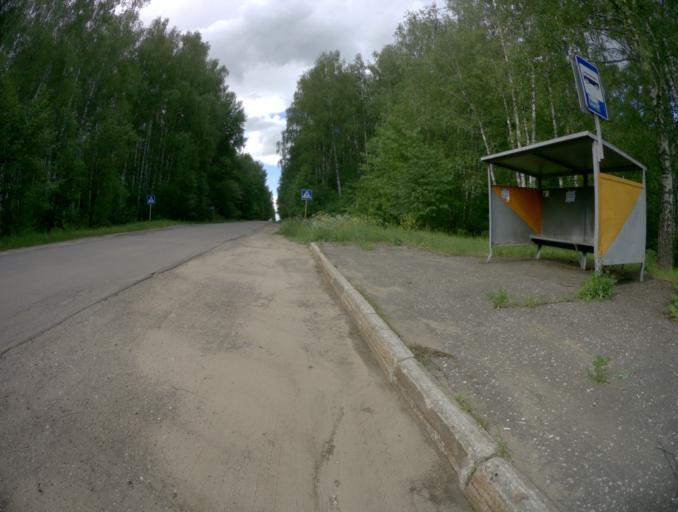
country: RU
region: Vladimir
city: Yur'yev-Pol'skiy
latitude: 56.4024
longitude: 39.7019
